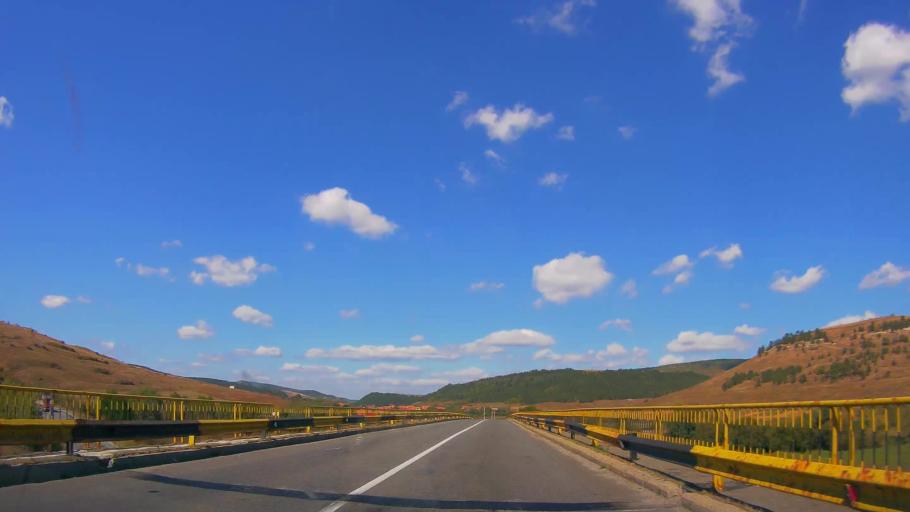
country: RO
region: Cluj
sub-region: Comuna Baciu
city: Mera
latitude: 46.8162
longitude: 23.4244
